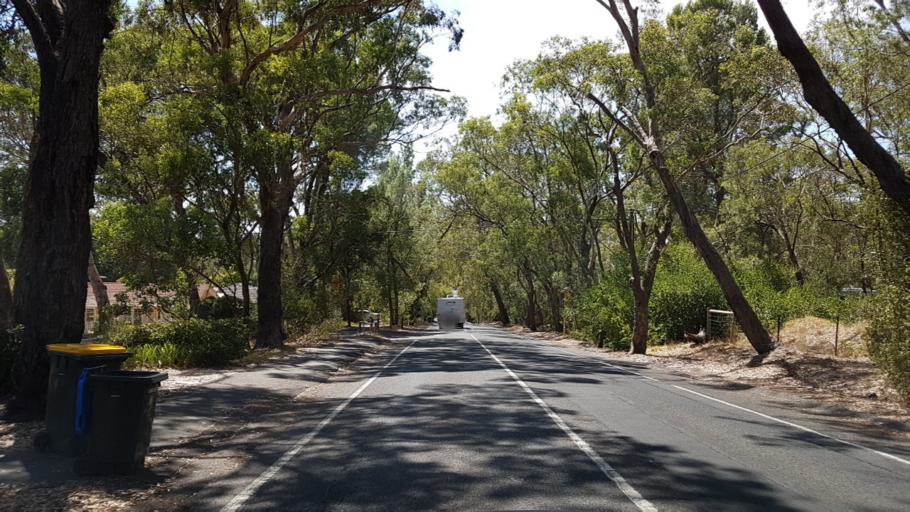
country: AU
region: South Australia
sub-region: Mitcham
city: Belair
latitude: -35.0117
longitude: 138.6334
